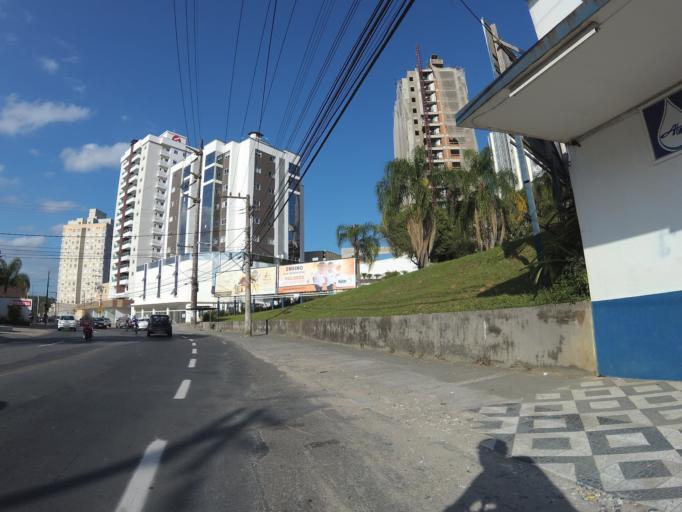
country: BR
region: Santa Catarina
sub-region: Blumenau
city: Blumenau
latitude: -26.9228
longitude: -49.0988
